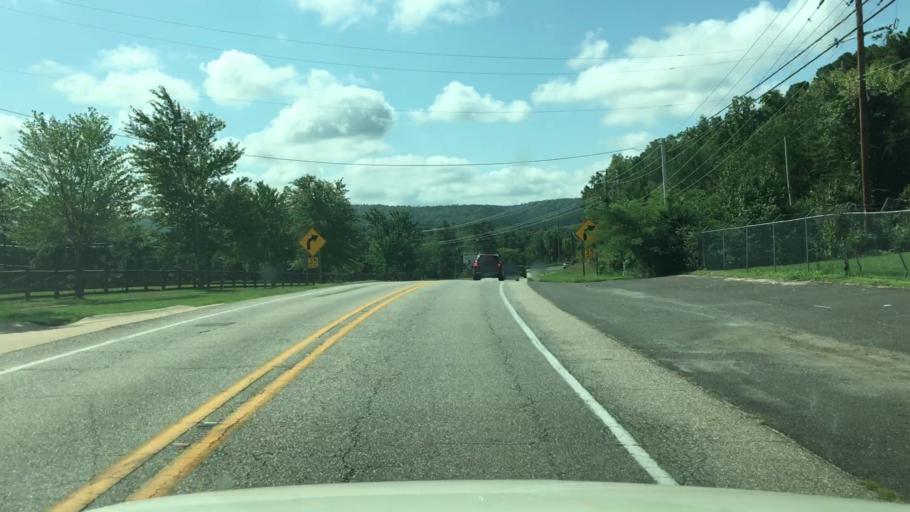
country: US
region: Arkansas
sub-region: Garland County
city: Lake Hamilton
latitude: 34.4073
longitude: -93.0913
